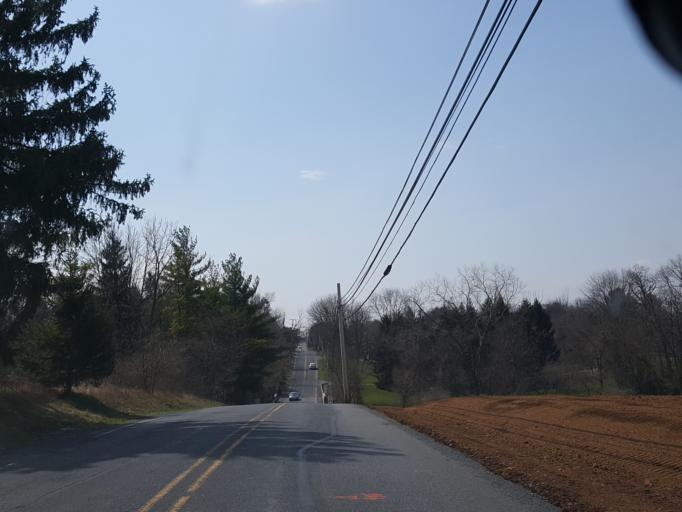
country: US
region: Pennsylvania
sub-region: Lebanon County
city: Annville
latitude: 40.3171
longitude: -76.5139
